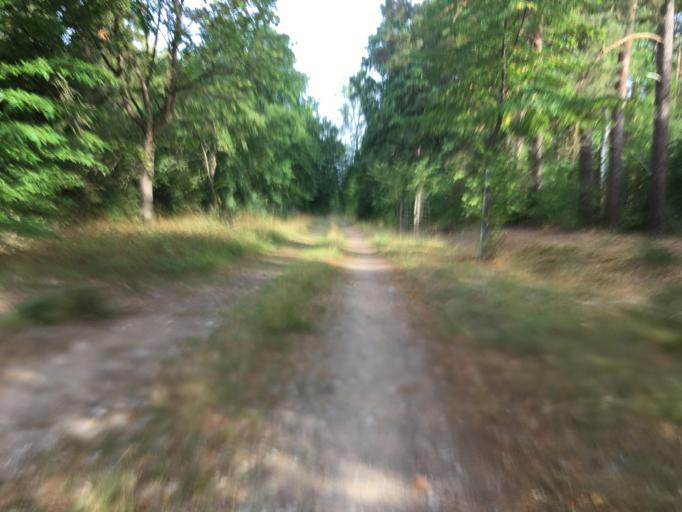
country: DE
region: Brandenburg
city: Marienwerder
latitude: 52.9723
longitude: 13.5306
